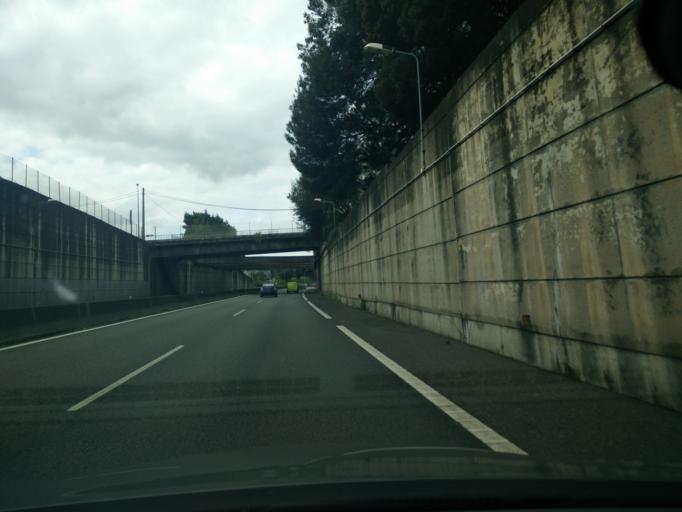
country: ES
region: Galicia
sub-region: Provincia da Coruna
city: Culleredo
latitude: 43.3133
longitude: -8.3822
